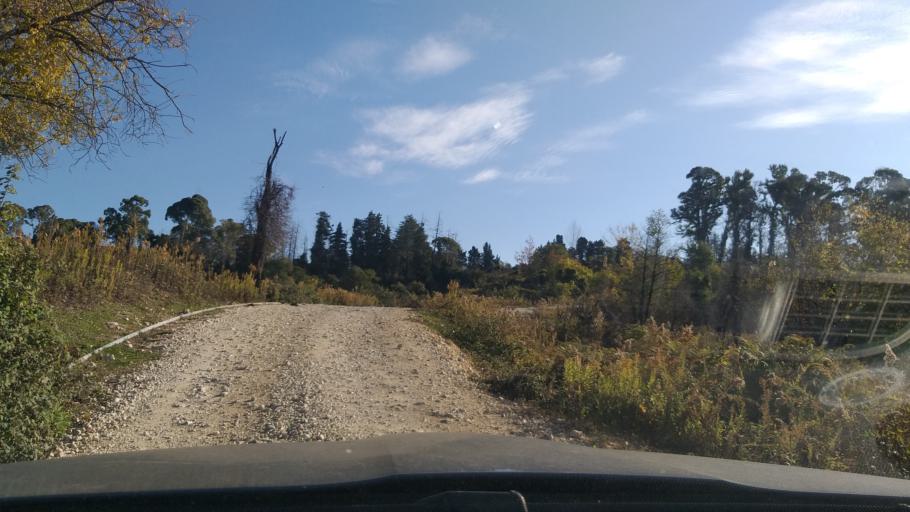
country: GE
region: Abkhazia
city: Stantsiya Novyy Afon
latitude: 43.0491
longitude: 40.9024
